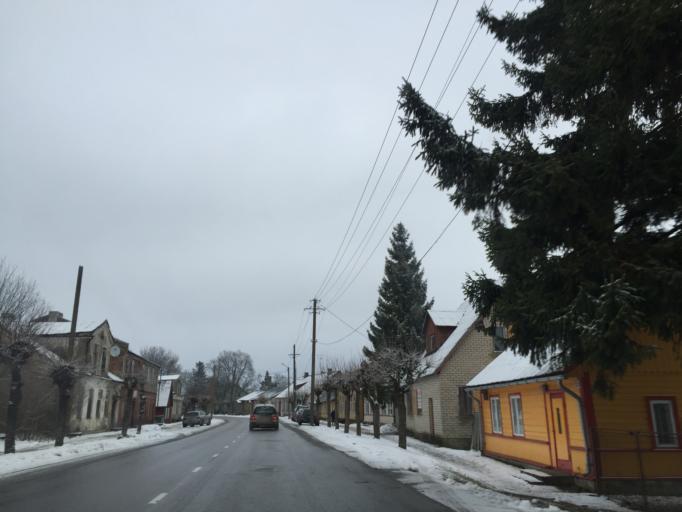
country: EE
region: Laeaene
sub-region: Lihula vald
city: Lihula
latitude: 58.6839
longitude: 23.8294
